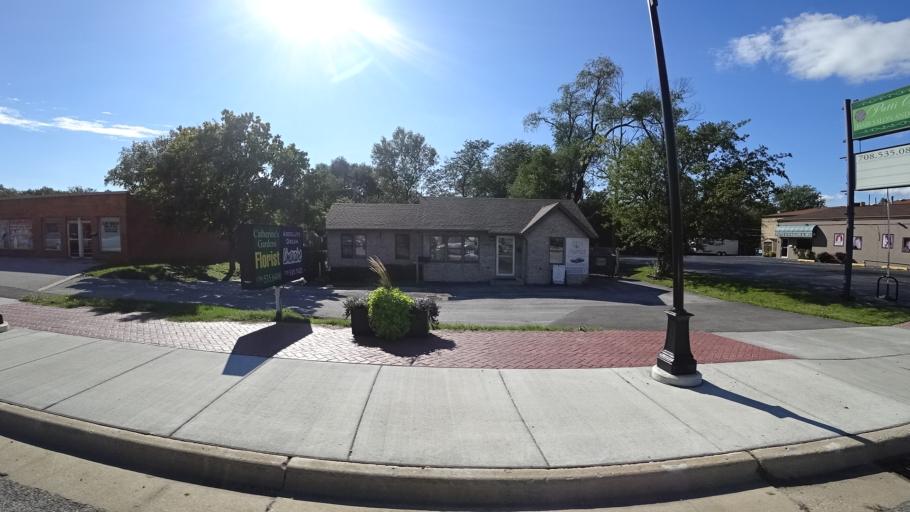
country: US
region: Illinois
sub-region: Cook County
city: Oak Forest
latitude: 41.6166
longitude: -87.7371
